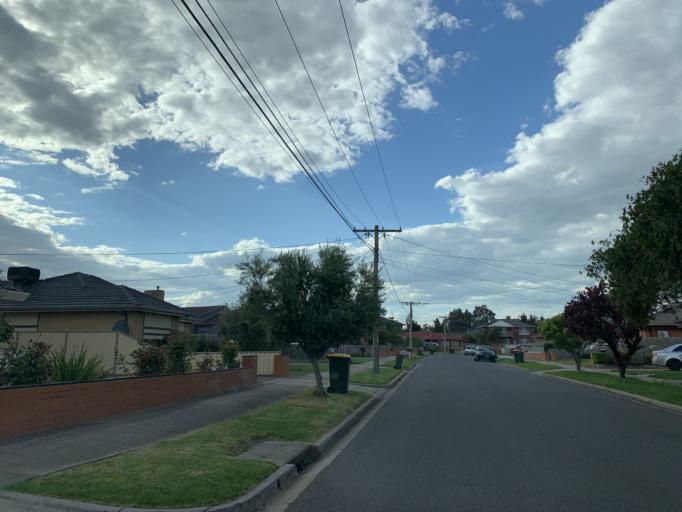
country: AU
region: Victoria
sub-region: Moonee Valley
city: Essendon West
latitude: -37.7547
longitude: 144.8598
